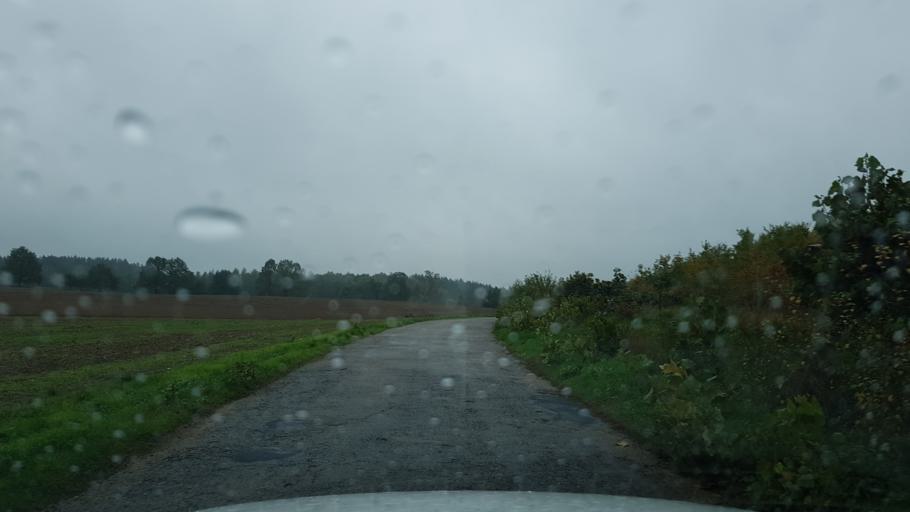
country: PL
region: West Pomeranian Voivodeship
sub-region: Powiat mysliborski
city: Barlinek
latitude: 53.0403
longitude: 15.2404
